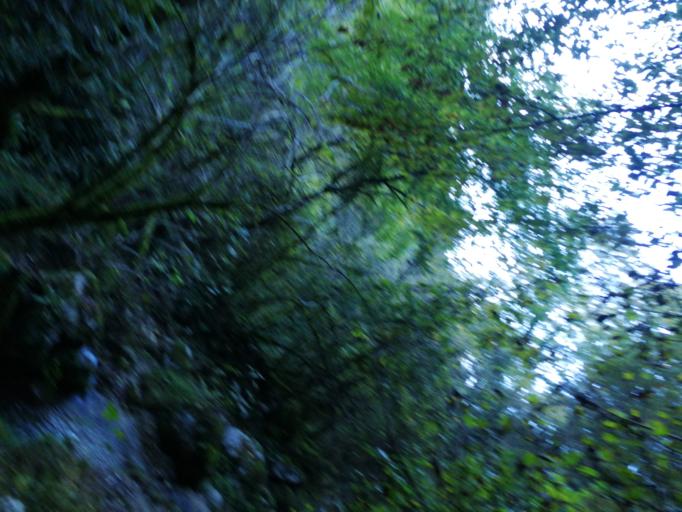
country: GE
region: Abkhazia
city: Gagra
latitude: 43.3254
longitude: 40.2554
